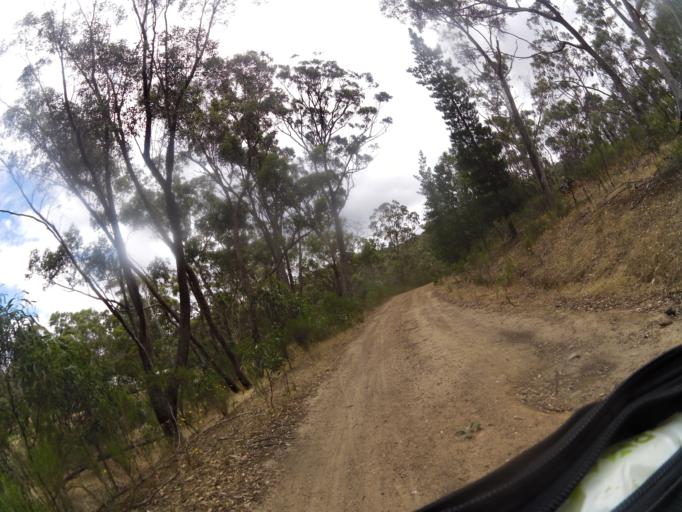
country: AU
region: Victoria
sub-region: Mount Alexander
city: Castlemaine
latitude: -37.0329
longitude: 144.2634
